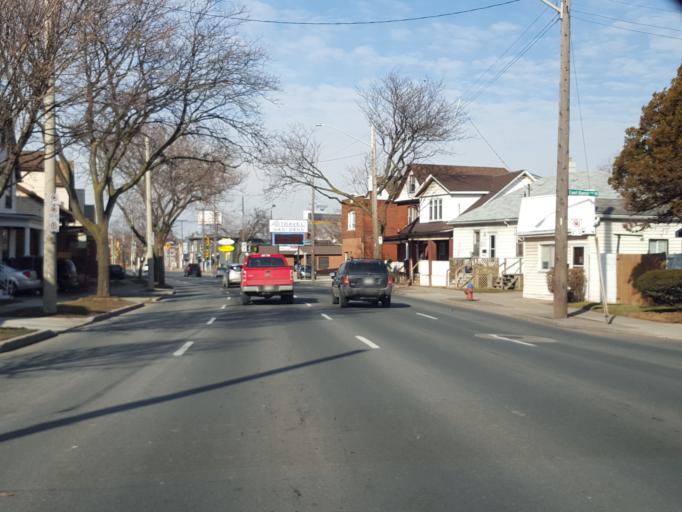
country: CA
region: Ontario
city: Hamilton
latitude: 43.2468
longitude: -79.8272
